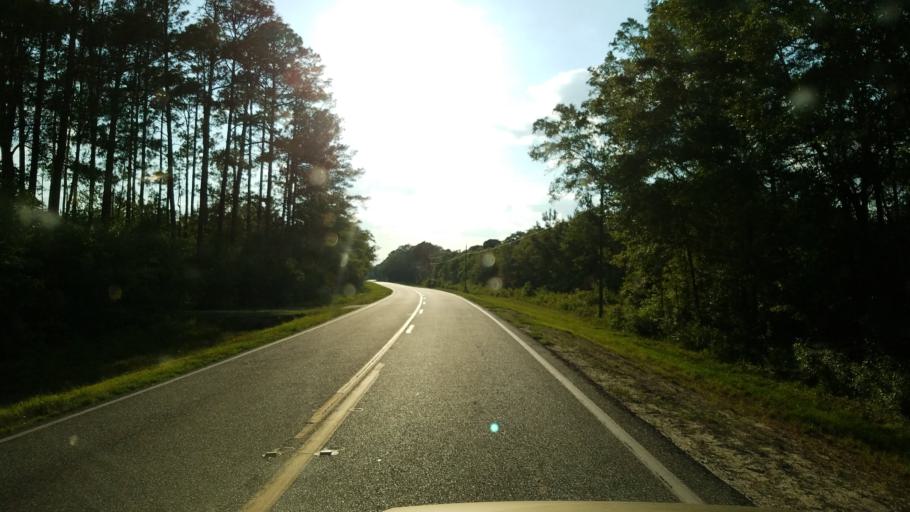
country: US
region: Georgia
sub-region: Berrien County
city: Nashville
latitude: 31.1782
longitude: -83.1278
